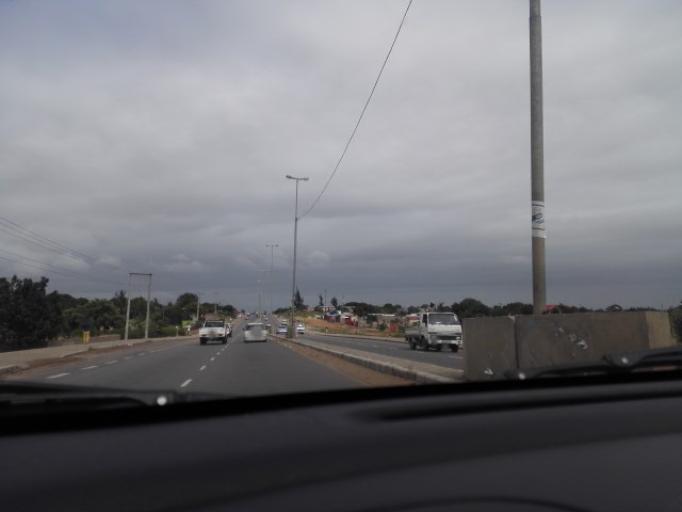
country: MZ
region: Maputo City
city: Maputo
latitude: -25.8246
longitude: 32.5955
